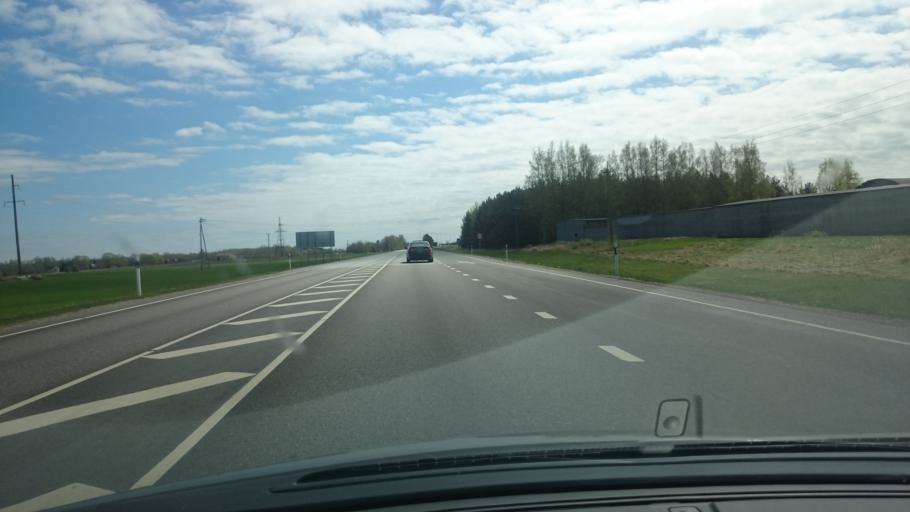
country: EE
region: Ida-Virumaa
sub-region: Kohtla-Jaerve linn
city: Kohtla-Jarve
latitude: 59.4098
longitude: 27.3124
